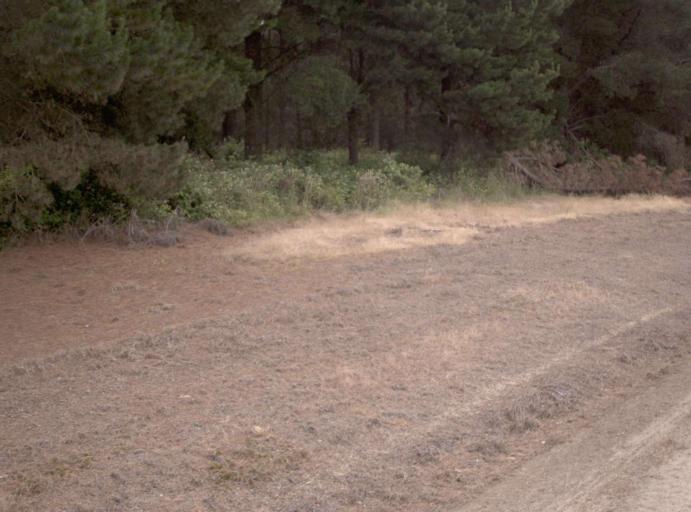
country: AU
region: Victoria
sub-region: Latrobe
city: Traralgon
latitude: -38.3922
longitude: 146.6599
